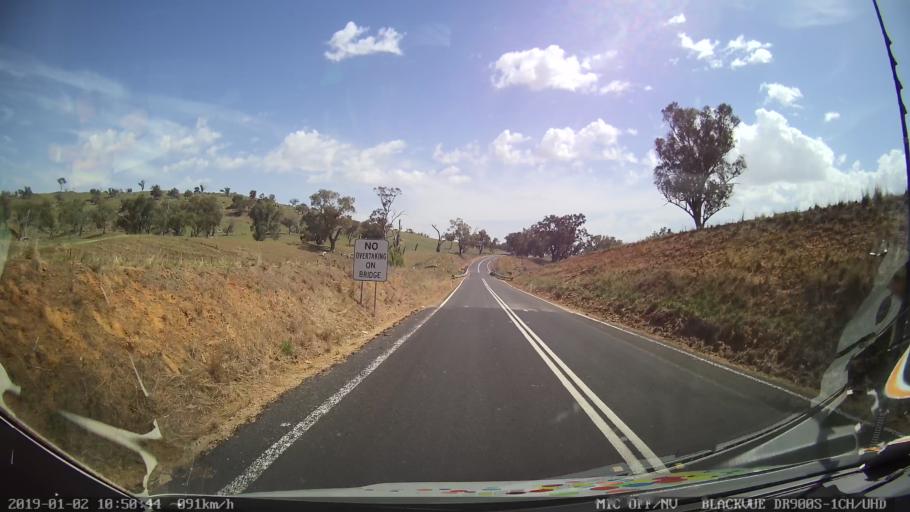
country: AU
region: New South Wales
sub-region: Cootamundra
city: Cootamundra
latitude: -34.7102
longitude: 148.2756
